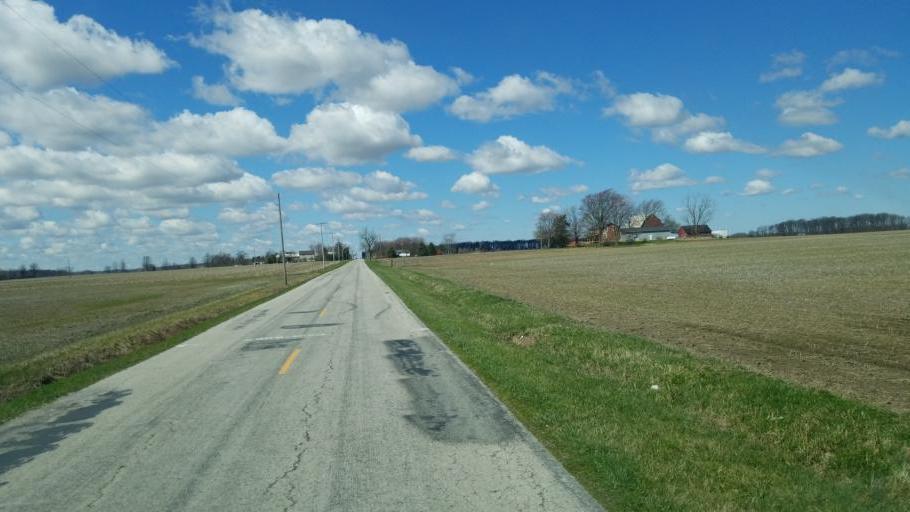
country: US
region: Ohio
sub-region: Sandusky County
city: Mount Carmel
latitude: 41.2419
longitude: -82.9596
